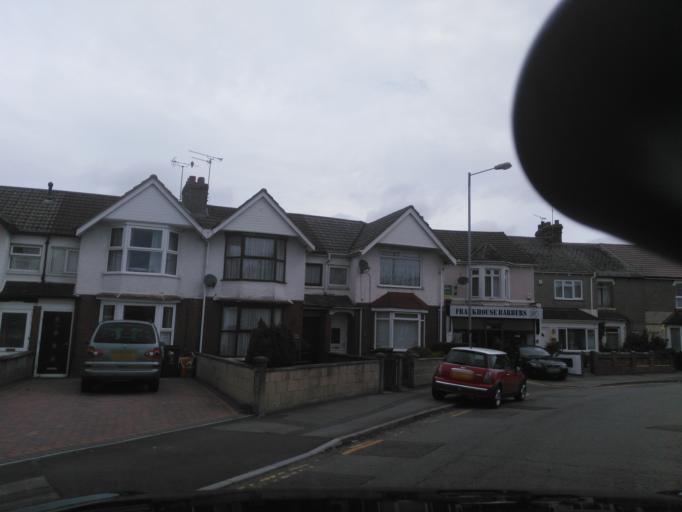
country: GB
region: England
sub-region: Borough of Swindon
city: Swindon
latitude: 51.5710
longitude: -1.7885
